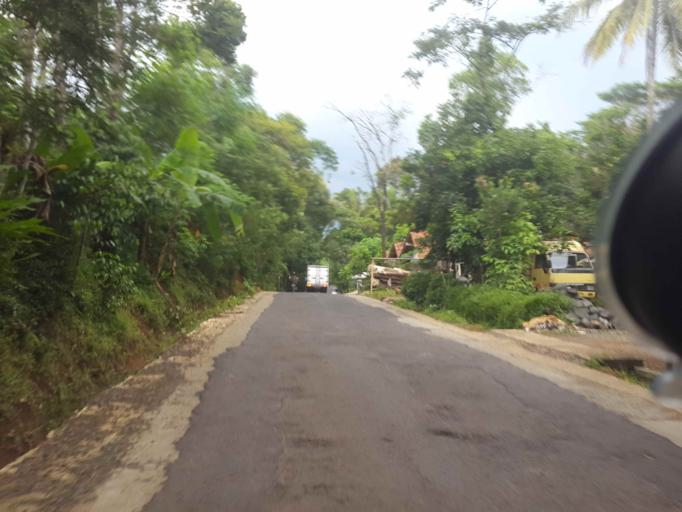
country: ID
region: Central Java
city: Banyumas
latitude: -7.5483
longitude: 109.3126
